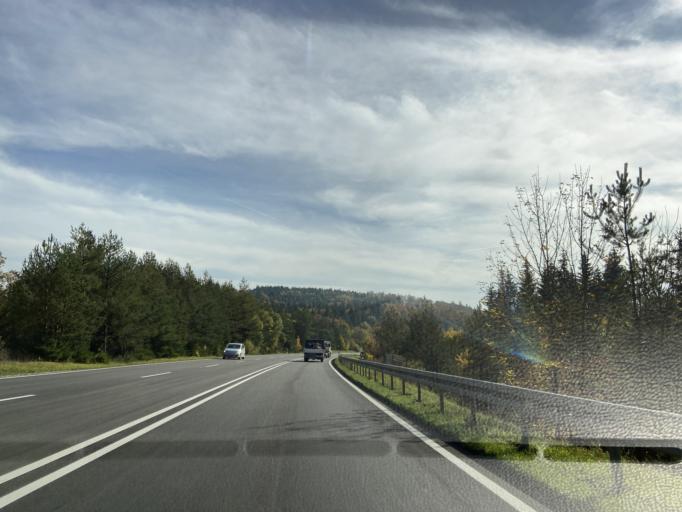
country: DE
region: Baden-Wuerttemberg
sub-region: Tuebingen Region
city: Sigmaringen
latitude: 48.1116
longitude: 9.2045
